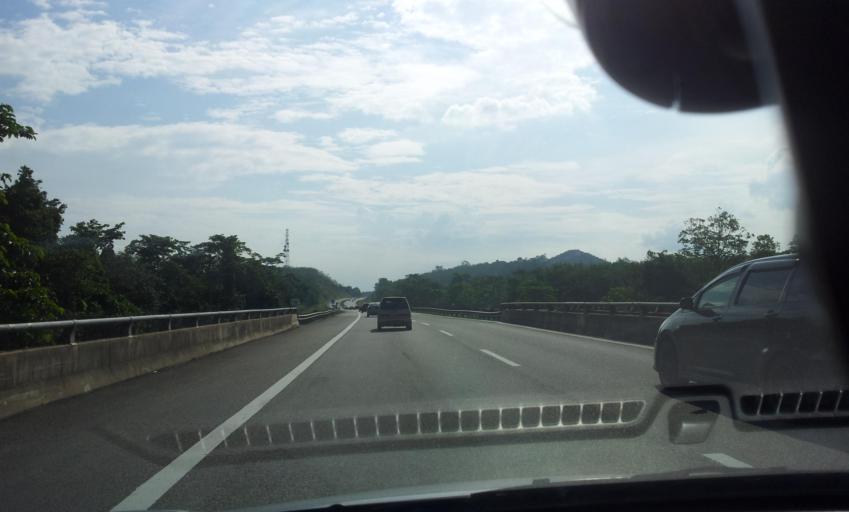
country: MY
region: Pahang
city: Mentekab
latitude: 3.5292
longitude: 102.2180
